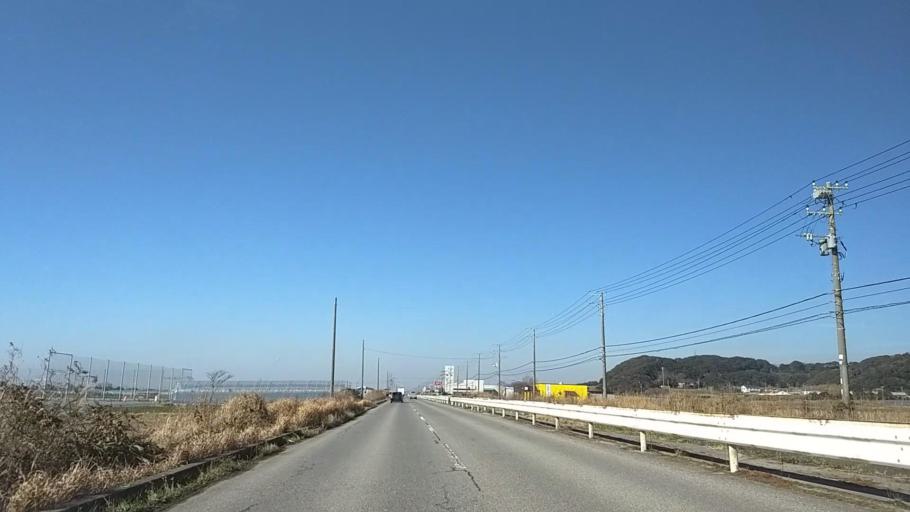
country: JP
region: Chiba
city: Asahi
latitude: 35.7122
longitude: 140.7137
